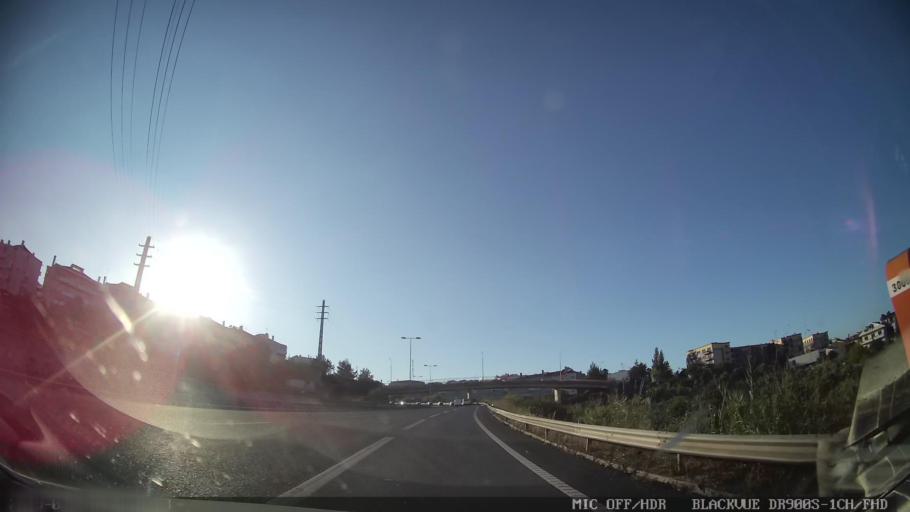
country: PT
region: Lisbon
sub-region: Loures
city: Santa Iria da Azoia
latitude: 38.8468
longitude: -9.0819
